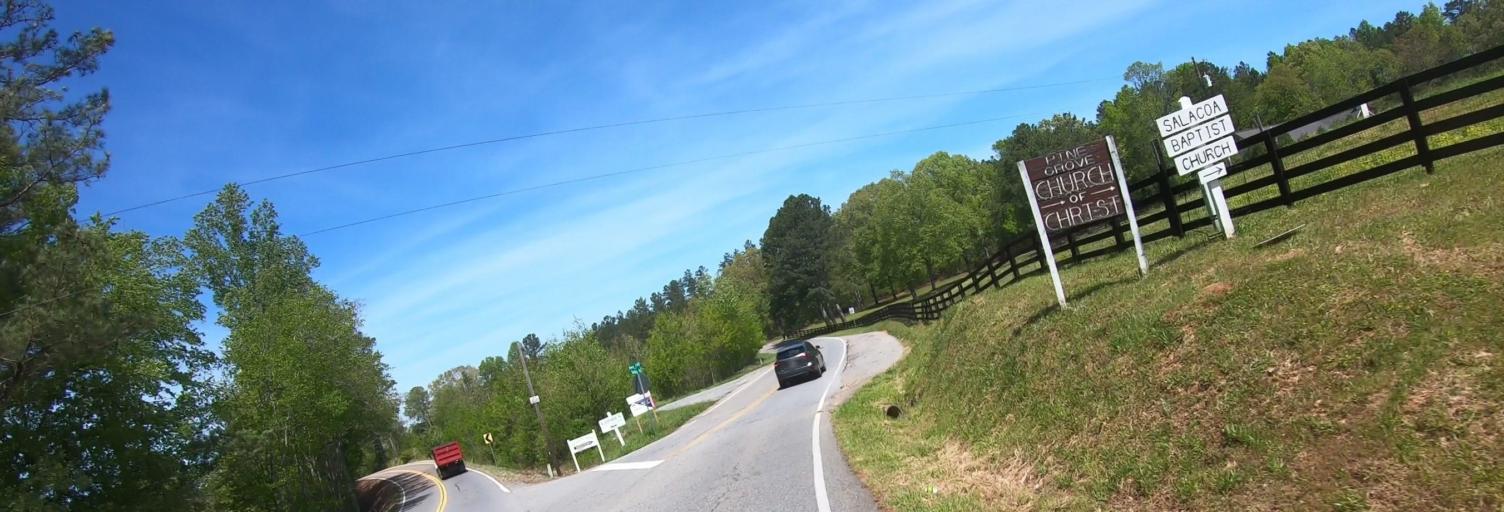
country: US
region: Georgia
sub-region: Bartow County
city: Rydal
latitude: 34.3459
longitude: -84.5797
